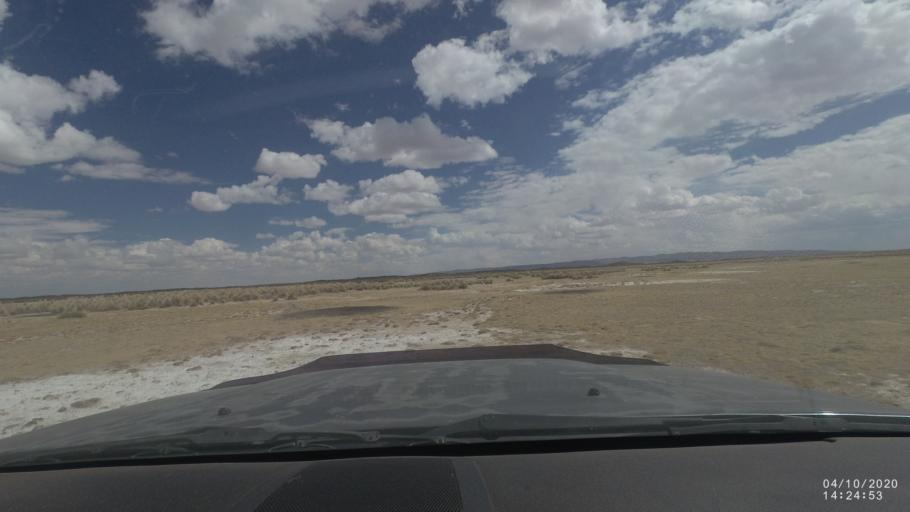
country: BO
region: Oruro
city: Poopo
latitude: -18.6770
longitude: -67.4510
